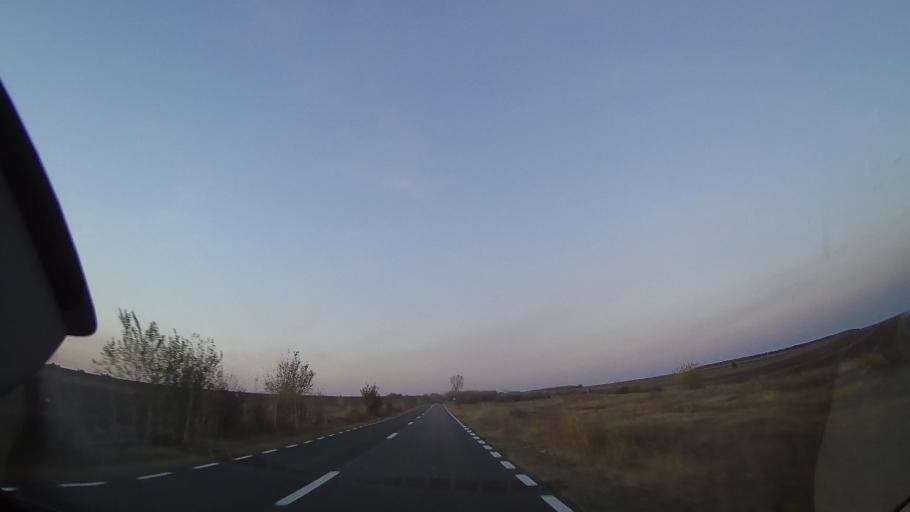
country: RO
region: Constanta
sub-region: Comuna Cobadin
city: Cobadin
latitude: 44.0293
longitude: 28.2620
